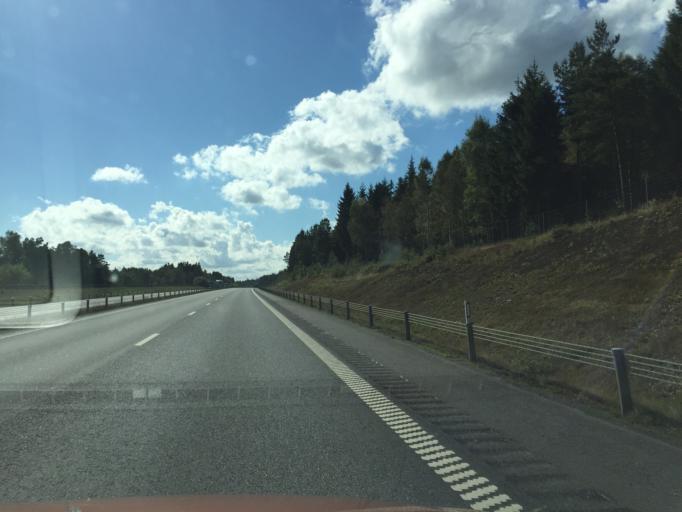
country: SE
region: Kronoberg
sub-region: Markaryds Kommun
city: Stromsnasbruk
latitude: 56.5392
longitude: 13.7006
